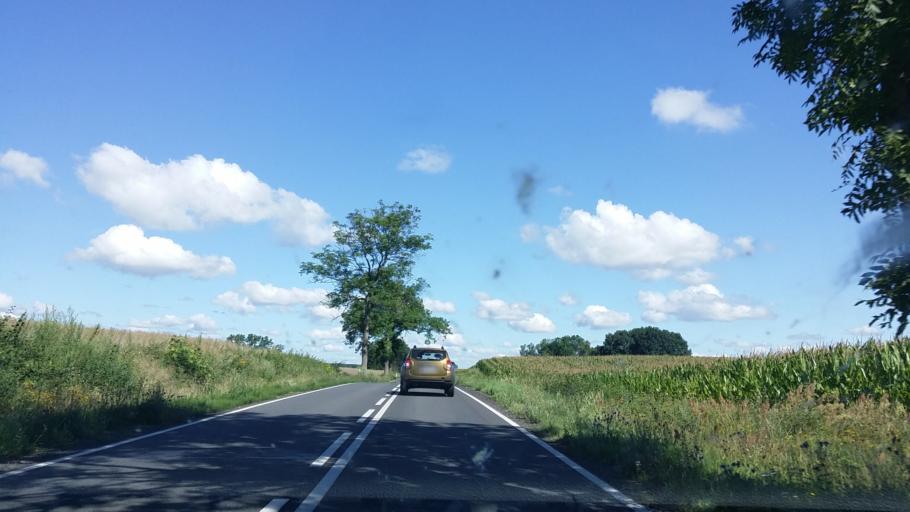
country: PL
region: West Pomeranian Voivodeship
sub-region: Powiat drawski
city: Kalisz Pomorski
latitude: 53.3204
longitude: 15.9037
